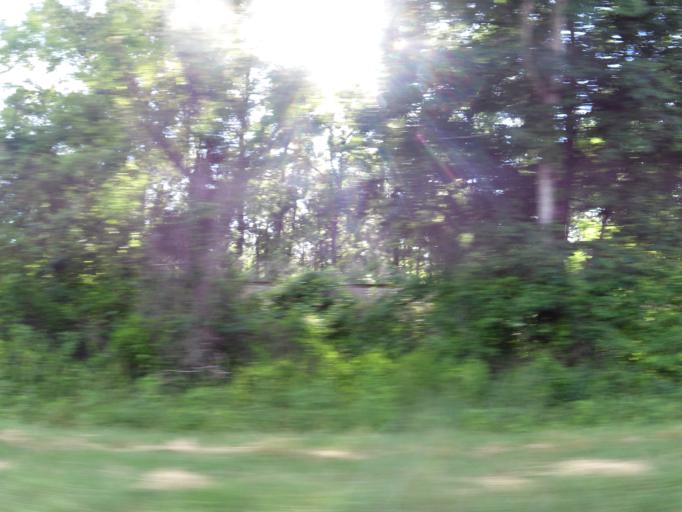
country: US
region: South Carolina
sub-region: Allendale County
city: Fairfax
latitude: 32.8834
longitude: -81.2383
